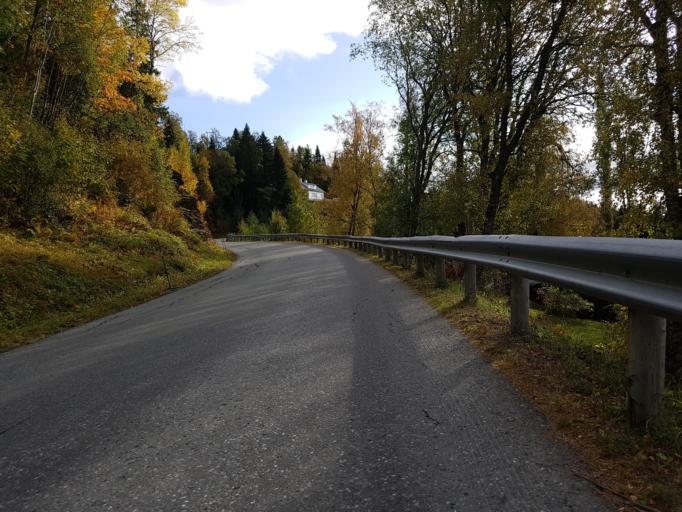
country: NO
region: Sor-Trondelag
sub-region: Klaebu
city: Klaebu
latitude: 63.3932
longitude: 10.5558
